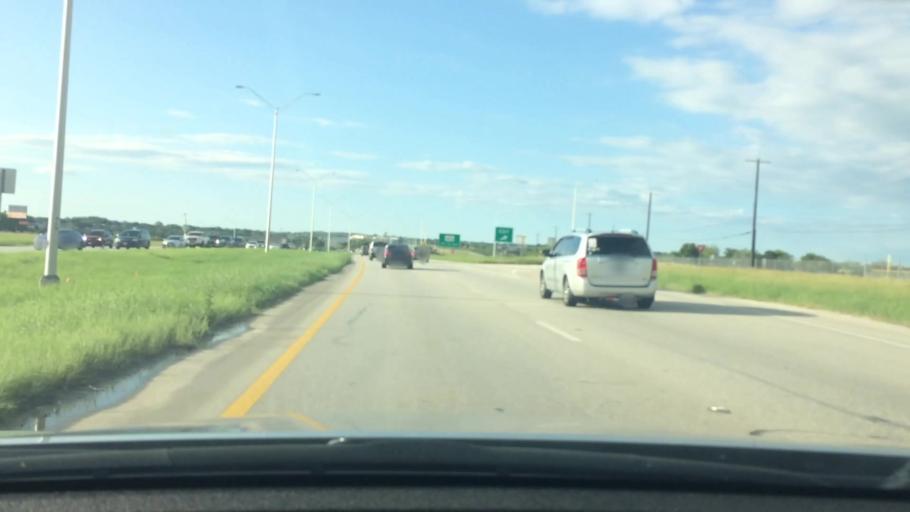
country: US
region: Texas
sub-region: Bexar County
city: Universal City
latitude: 29.5290
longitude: -98.2982
